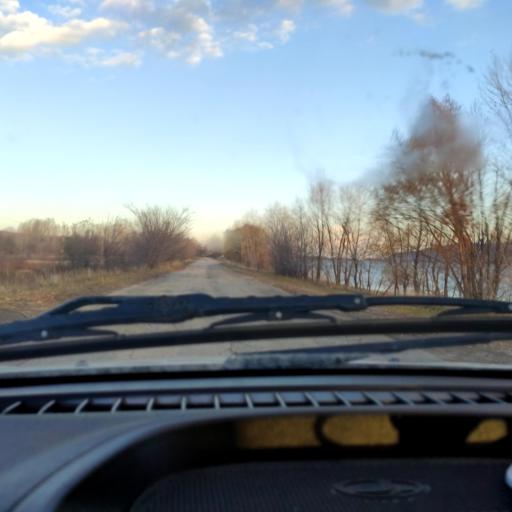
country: RU
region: Samara
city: Povolzhskiy
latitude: 53.4657
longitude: 49.6806
